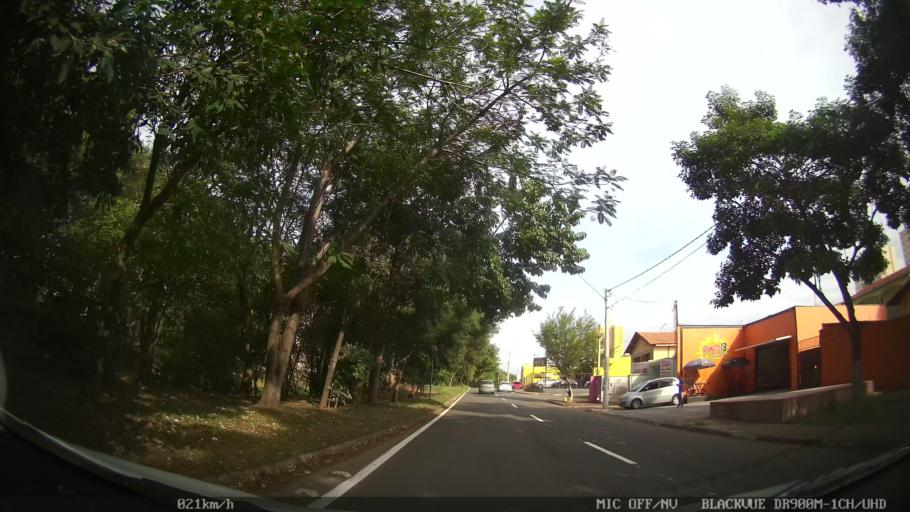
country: BR
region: Sao Paulo
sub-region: Piracicaba
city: Piracicaba
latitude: -22.7205
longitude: -47.6249
